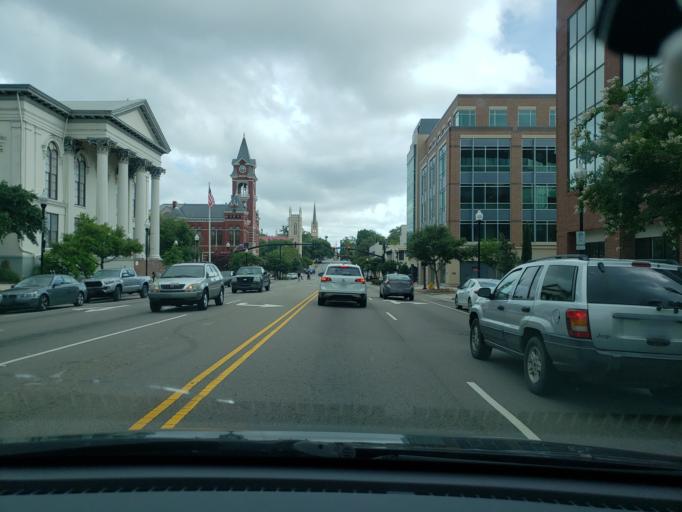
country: US
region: North Carolina
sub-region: New Hanover County
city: Wilmington
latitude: 34.2376
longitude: -77.9464
